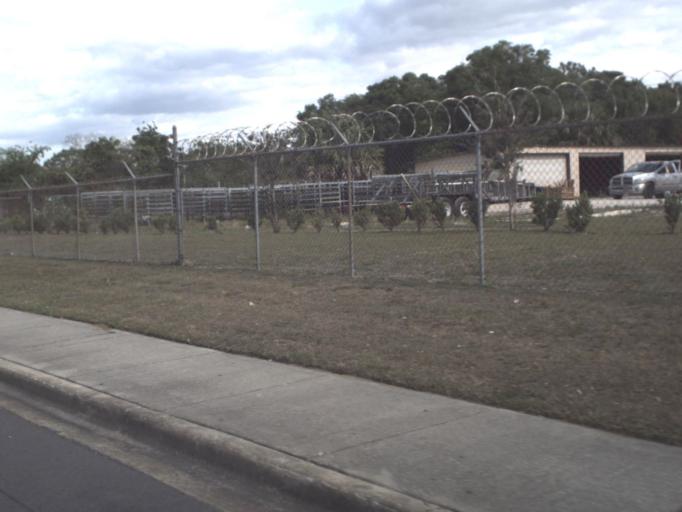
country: US
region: Florida
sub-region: Marion County
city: Ocala
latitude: 29.1969
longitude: -82.1539
